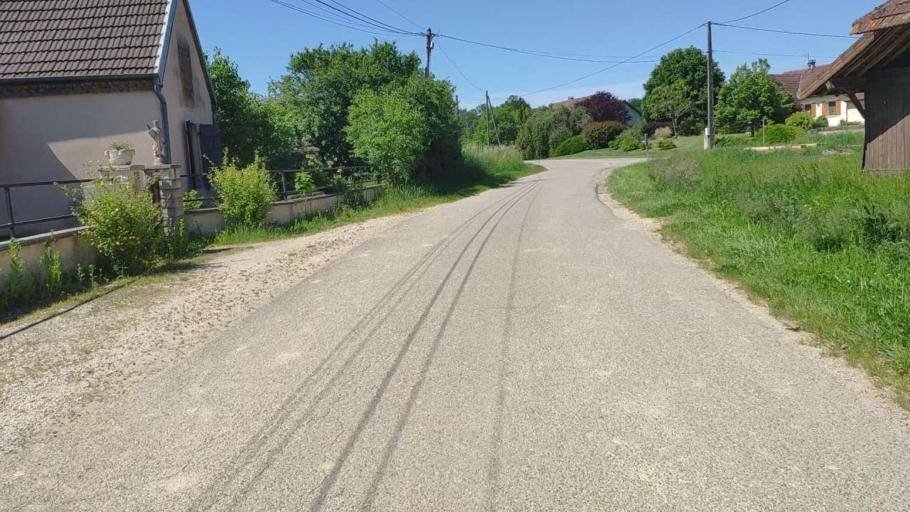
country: FR
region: Franche-Comte
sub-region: Departement du Jura
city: Bletterans
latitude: 46.7766
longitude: 5.4151
